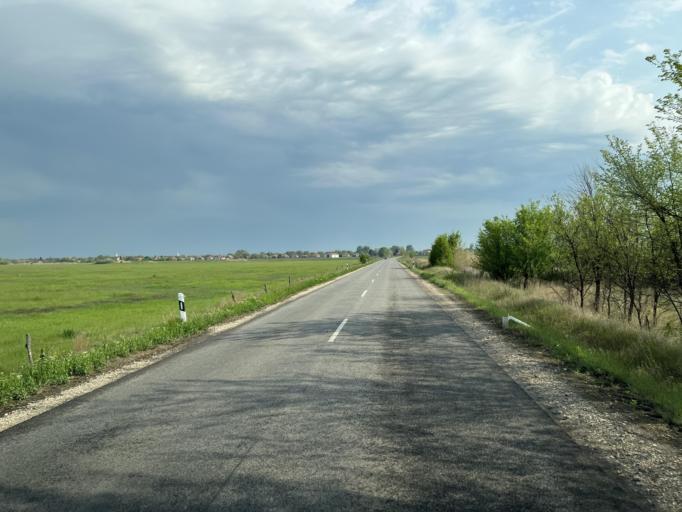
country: HU
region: Pest
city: Tapioszentmarton
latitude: 47.3228
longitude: 19.7498
